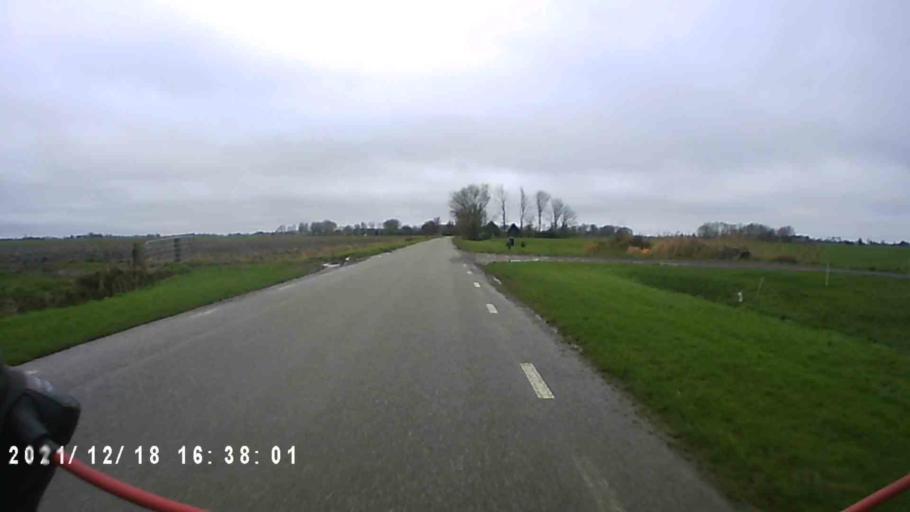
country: NL
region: Friesland
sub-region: Gemeente Dongeradeel
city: Dokkum
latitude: 53.3583
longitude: 6.0139
